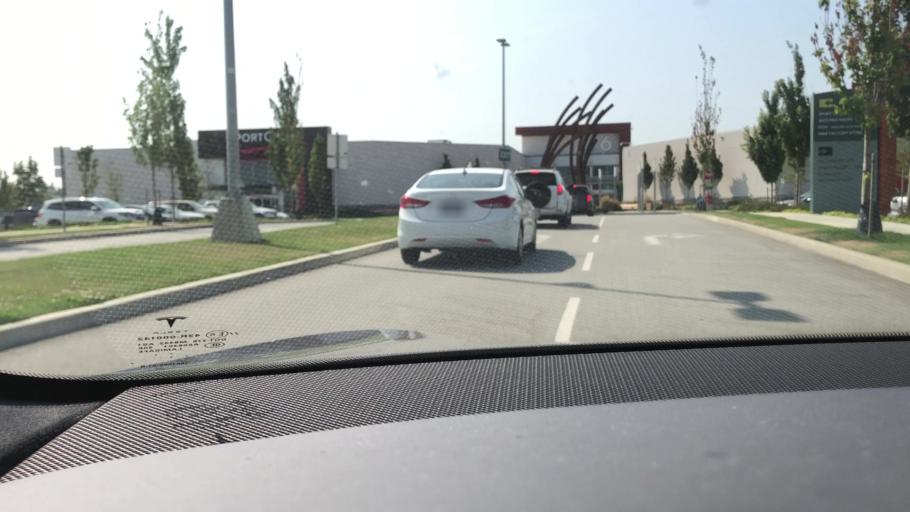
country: CA
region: British Columbia
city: Ladner
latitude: 49.0410
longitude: -123.0828
